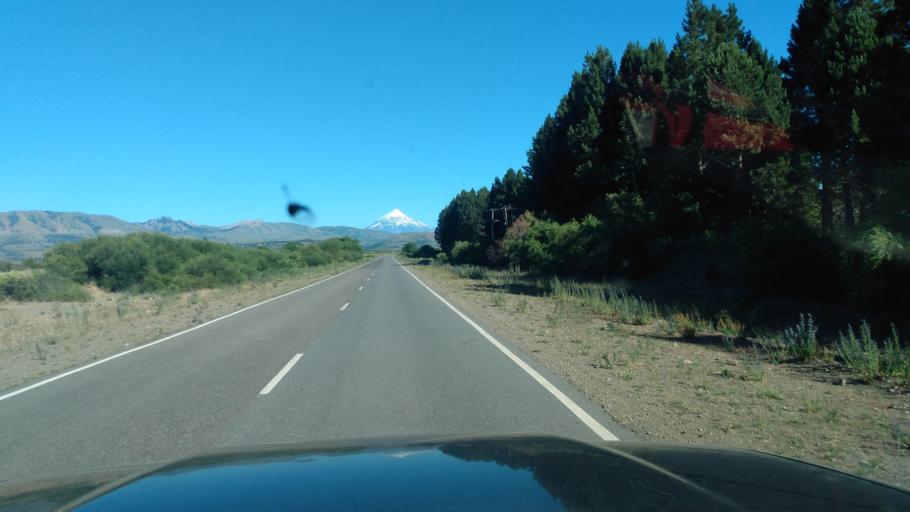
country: AR
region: Neuquen
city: Junin de los Andes
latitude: -39.8958
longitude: -71.1460
